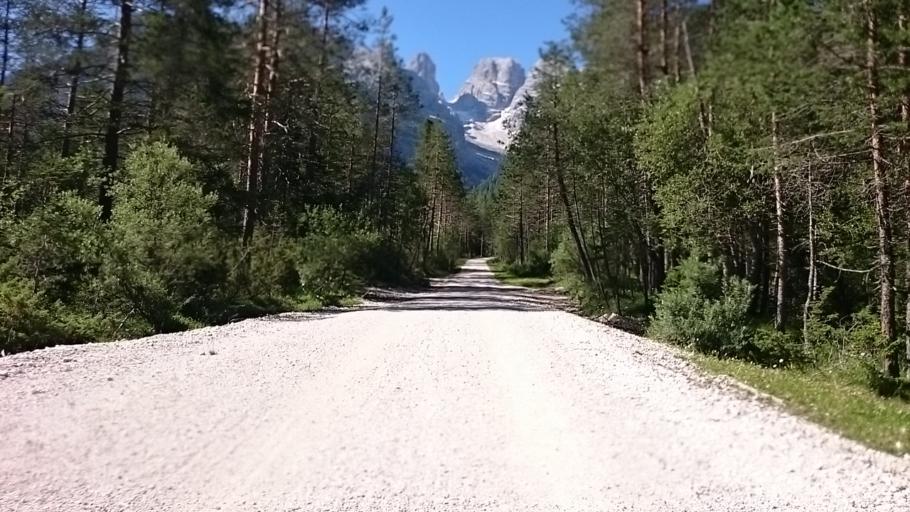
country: IT
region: Trentino-Alto Adige
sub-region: Bolzano
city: Dobbiaco
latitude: 46.6205
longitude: 12.2230
